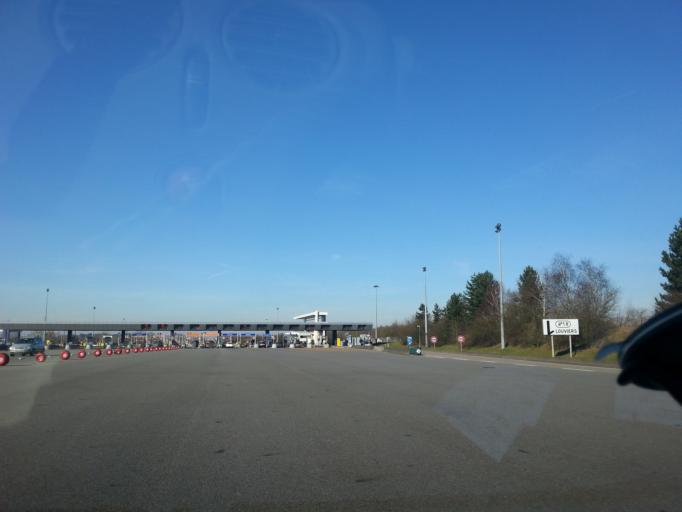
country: FR
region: Haute-Normandie
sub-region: Departement de l'Eure
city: Ande
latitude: 49.1900
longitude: 1.2336
